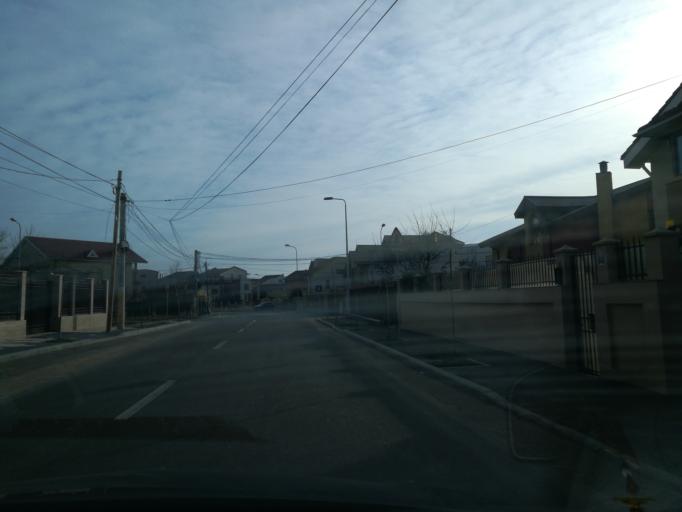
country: RO
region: Constanta
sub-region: Municipiul Constanta
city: Constanta
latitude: 44.1817
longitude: 28.6117
